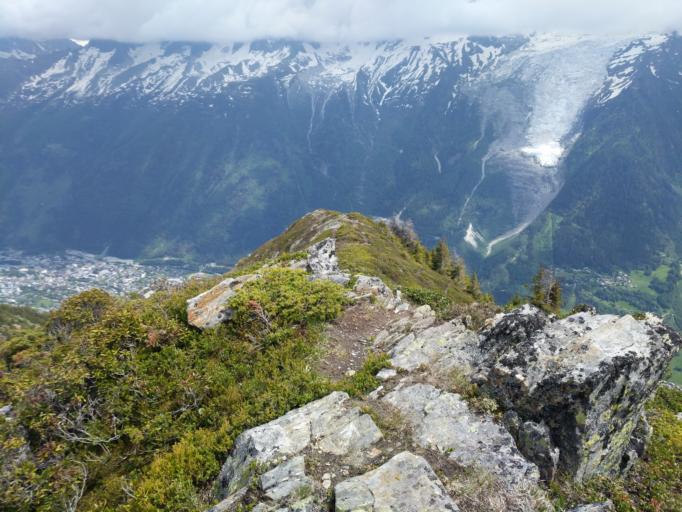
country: FR
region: Rhone-Alpes
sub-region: Departement de la Haute-Savoie
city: Les Houches
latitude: 45.9196
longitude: 6.8213
